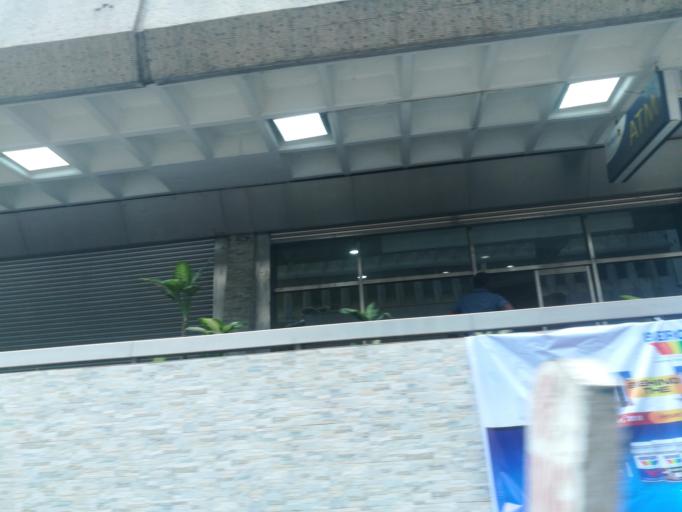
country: NG
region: Lagos
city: Lagos
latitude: 6.4532
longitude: 3.3884
